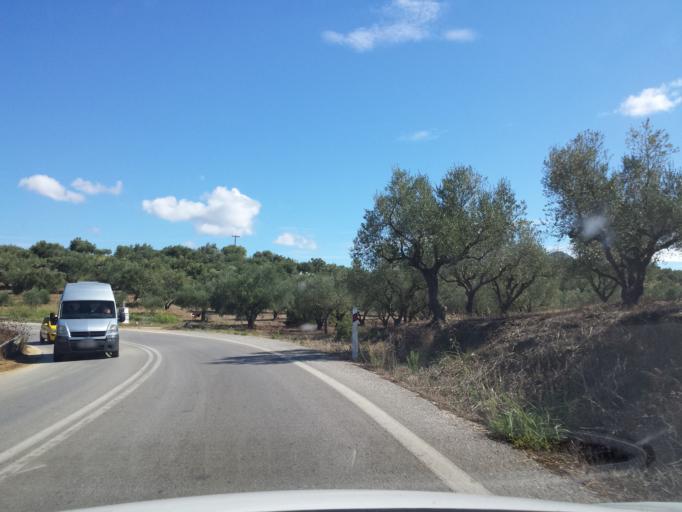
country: GR
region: Peloponnese
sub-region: Nomos Messinias
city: Pylos
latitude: 36.9451
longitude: 21.7580
